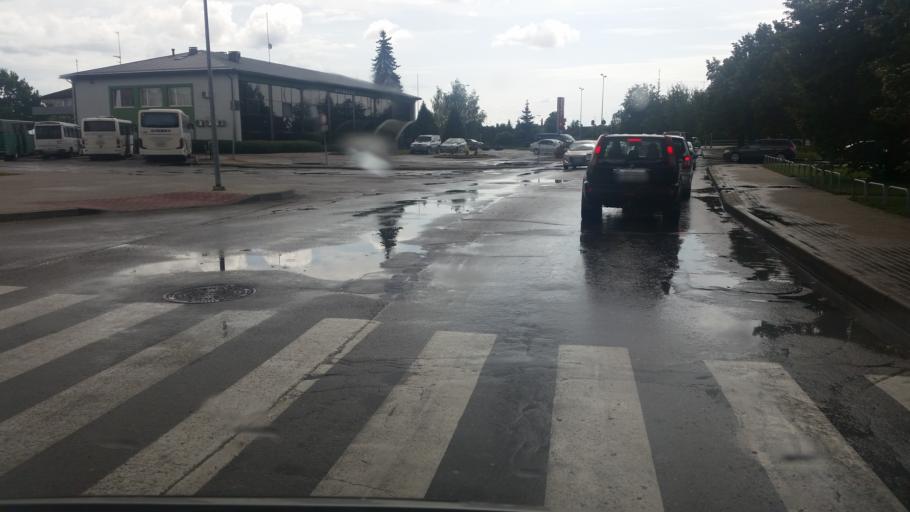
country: LV
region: Bauskas Rajons
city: Bauska
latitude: 56.4076
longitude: 24.1952
